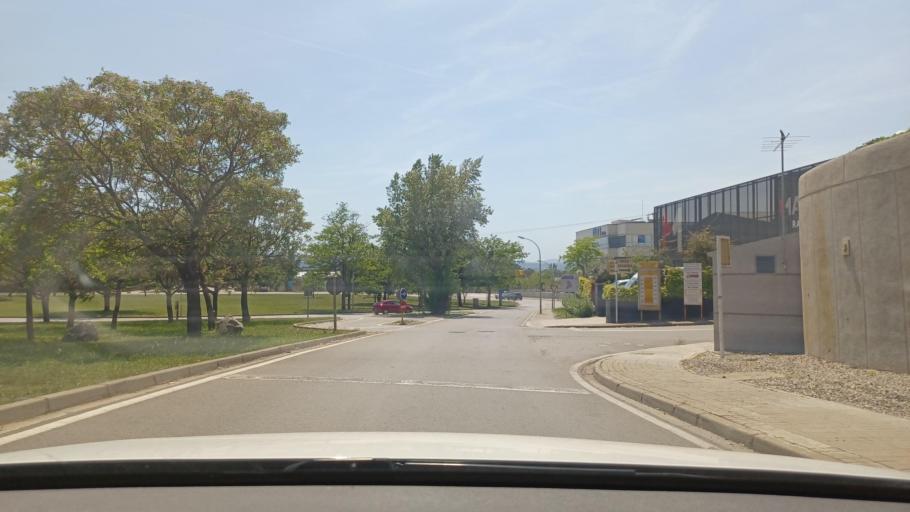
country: ES
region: Catalonia
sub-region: Provincia de Barcelona
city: Polinya
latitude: 41.5252
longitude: 2.1479
